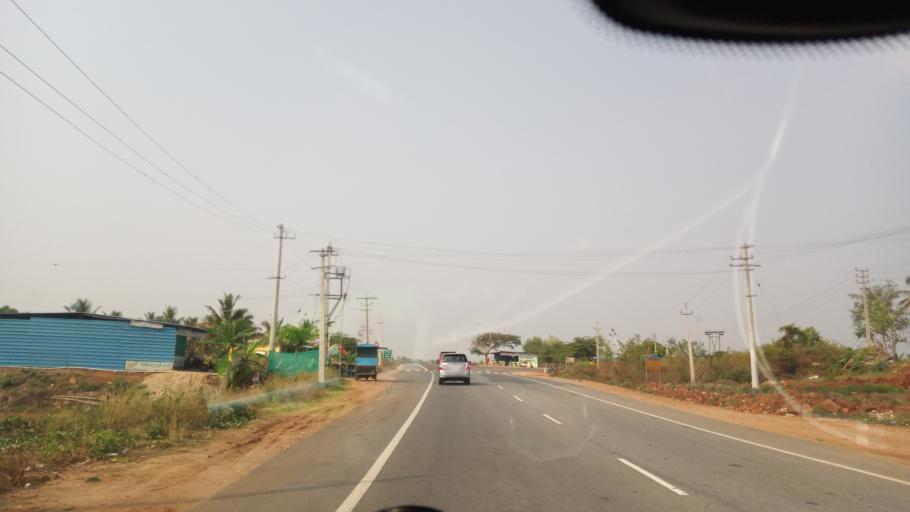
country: IN
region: Karnataka
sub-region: Mandya
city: Melukote
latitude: 12.7212
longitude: 76.7109
